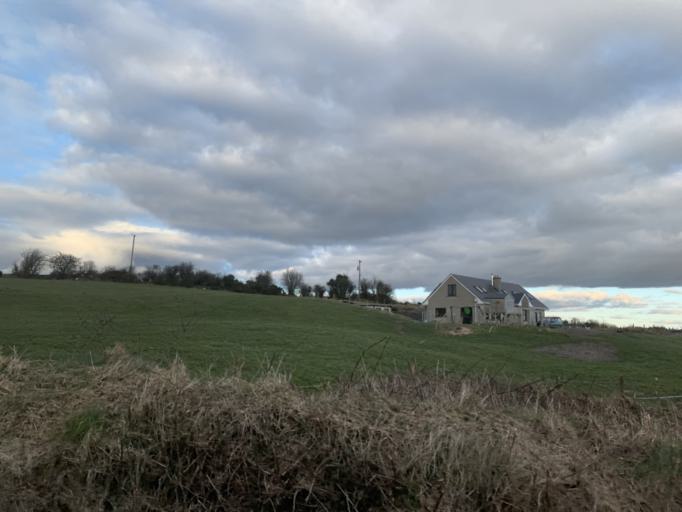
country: IE
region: Connaught
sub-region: Maigh Eo
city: Ballyhaunis
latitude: 53.8402
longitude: -8.7222
